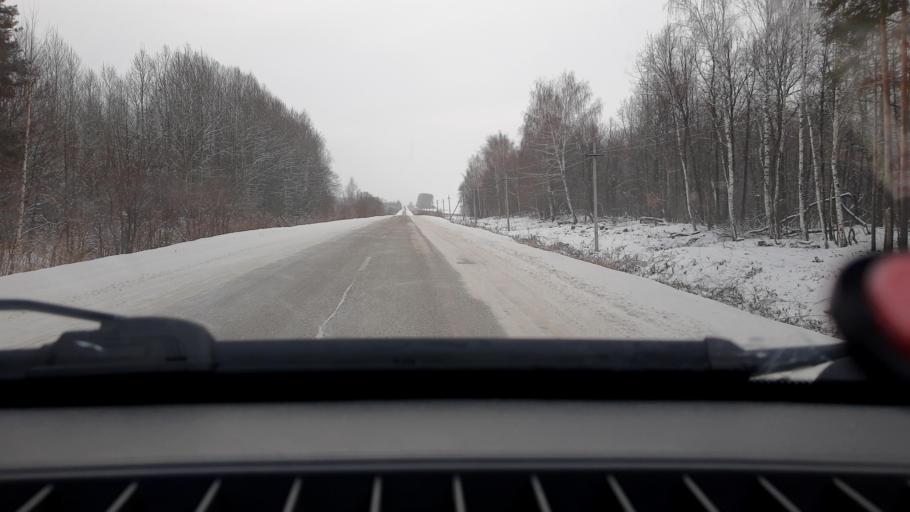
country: RU
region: Bashkortostan
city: Iglino
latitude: 54.6745
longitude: 56.4193
